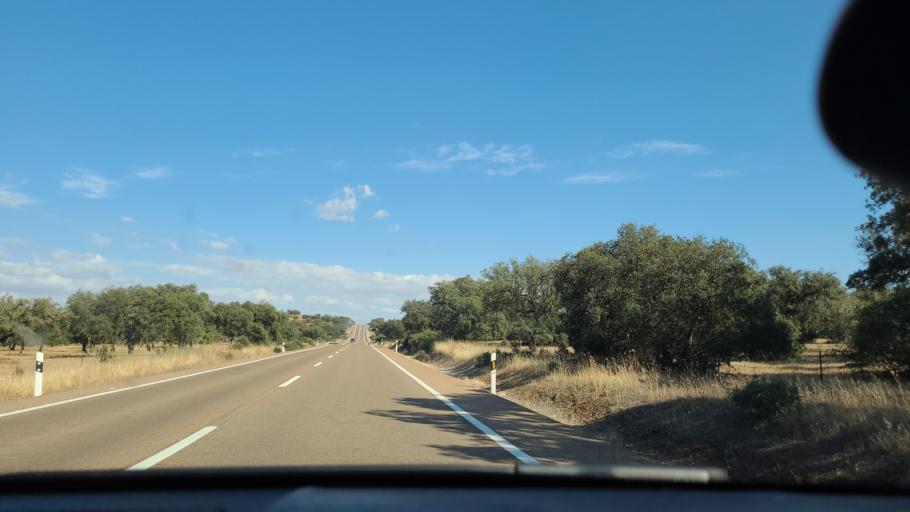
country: ES
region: Extremadura
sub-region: Provincia de Badajoz
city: Usagre
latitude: 38.3683
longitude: -6.2409
